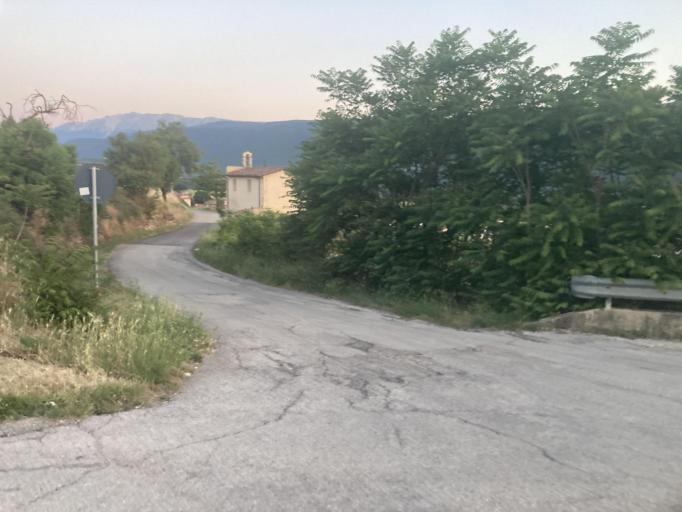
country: IT
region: Abruzzo
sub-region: Provincia dell' Aquila
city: San Demetrio Ne' Vestini
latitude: 42.2937
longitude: 13.5520
